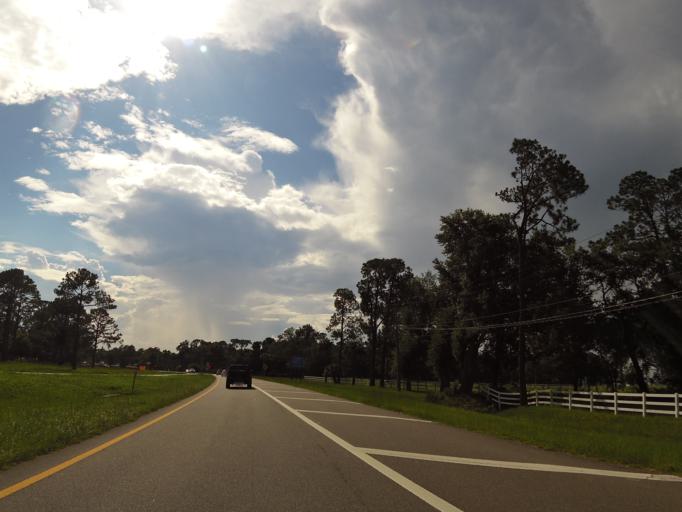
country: US
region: Florida
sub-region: Clay County
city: Green Cove Springs
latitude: 29.9846
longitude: -81.6614
